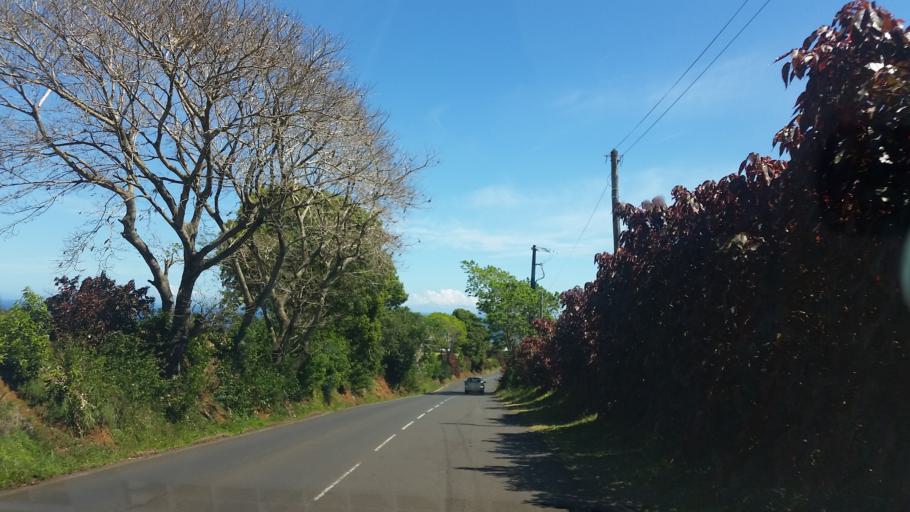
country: RE
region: Reunion
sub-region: Reunion
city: Sainte-Marie
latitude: -20.9295
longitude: 55.5308
